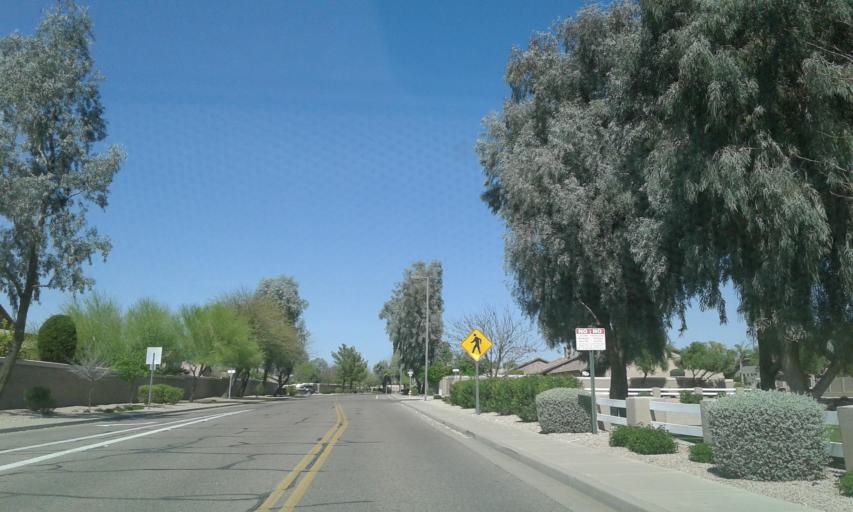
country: US
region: Arizona
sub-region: Maricopa County
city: Paradise Valley
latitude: 33.6481
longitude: -111.9687
